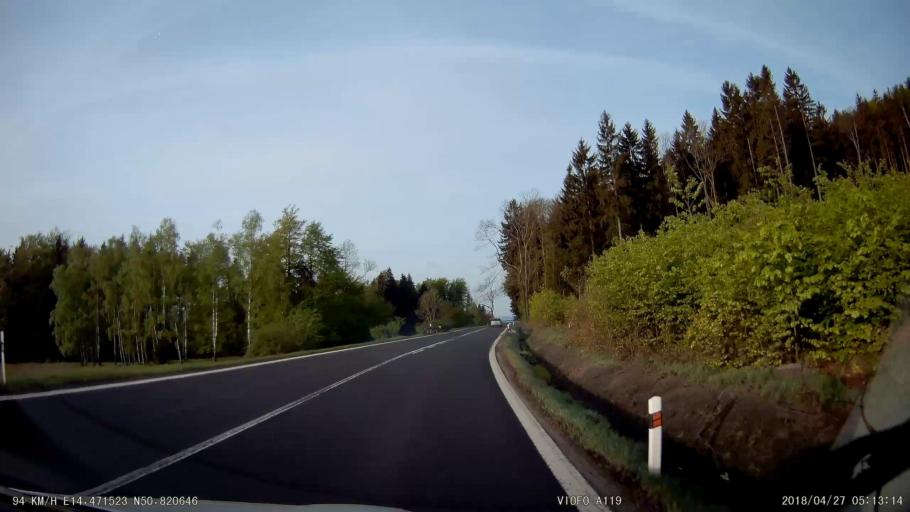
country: CZ
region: Ustecky
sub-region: Okres Decin
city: Chribska
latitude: 50.8203
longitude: 14.4714
